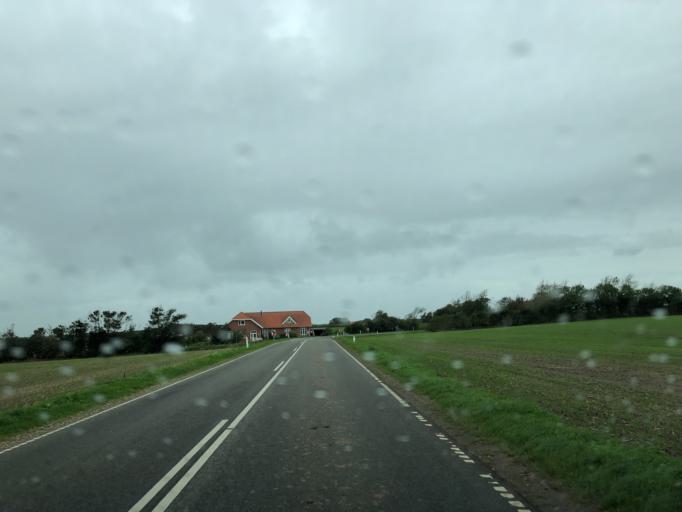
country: DK
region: North Denmark
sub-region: Thisted Kommune
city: Hurup
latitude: 56.7157
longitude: 8.3915
